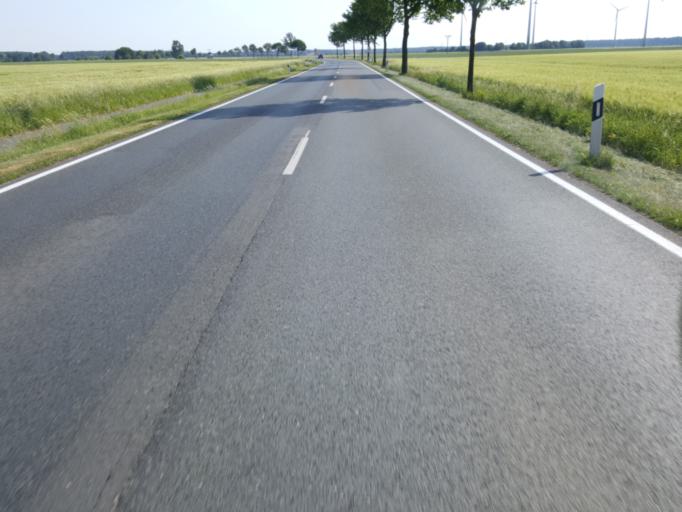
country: DE
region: Lower Saxony
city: Landesbergen
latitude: 52.5672
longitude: 9.1309
